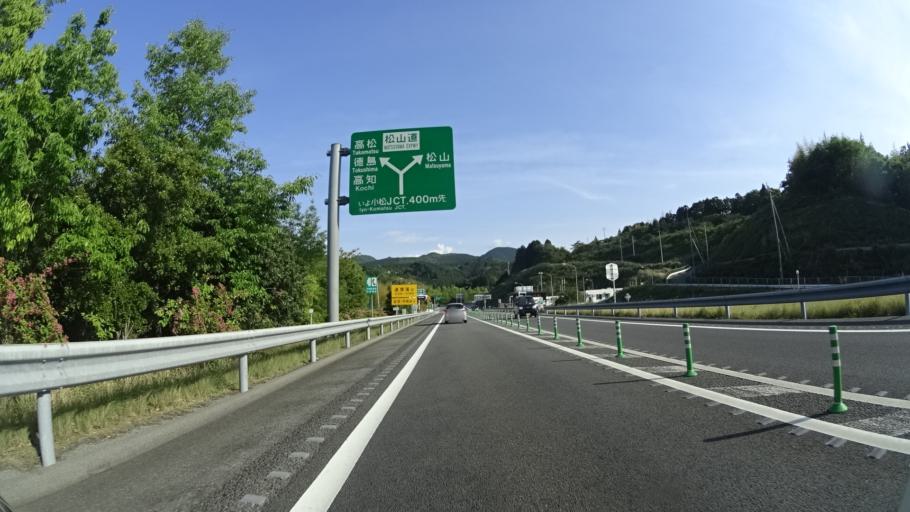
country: JP
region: Ehime
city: Saijo
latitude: 33.8870
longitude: 133.0873
